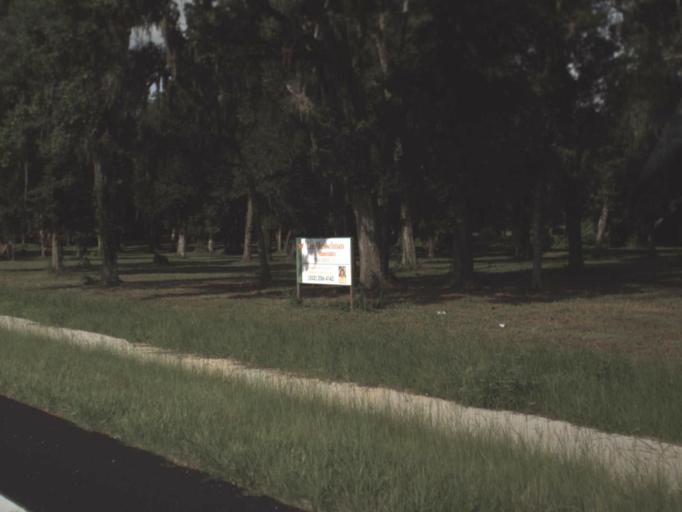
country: US
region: Florida
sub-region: Pasco County
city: Lacoochee
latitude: 28.4431
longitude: -82.1895
